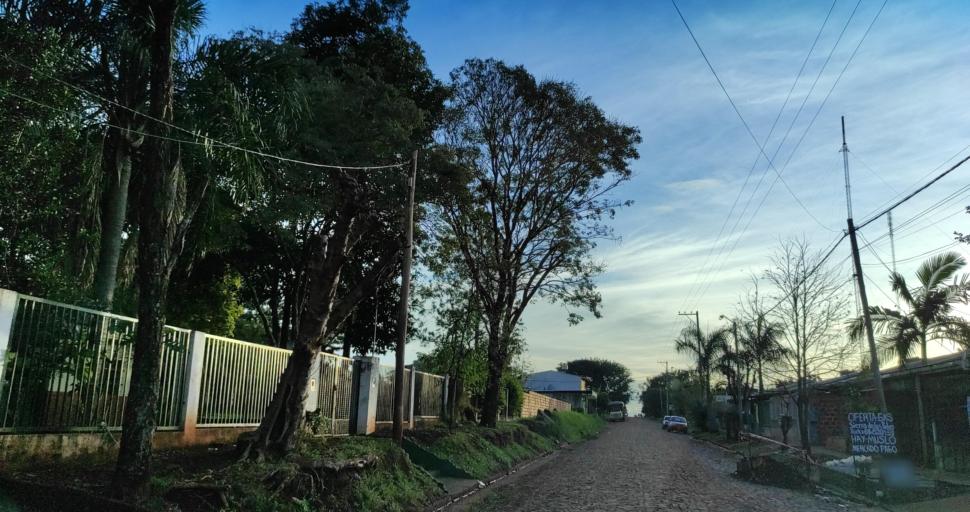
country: AR
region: Misiones
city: Garupa
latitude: -27.4791
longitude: -55.8576
